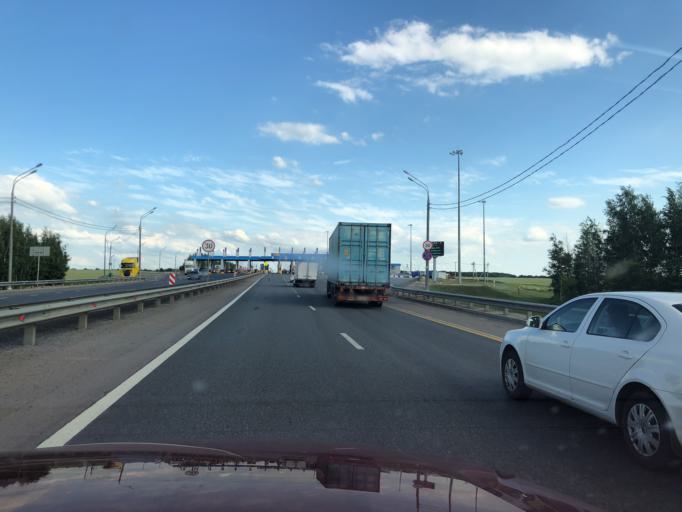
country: RU
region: Lipetsk
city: Zadonsk
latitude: 52.4319
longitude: 38.8225
